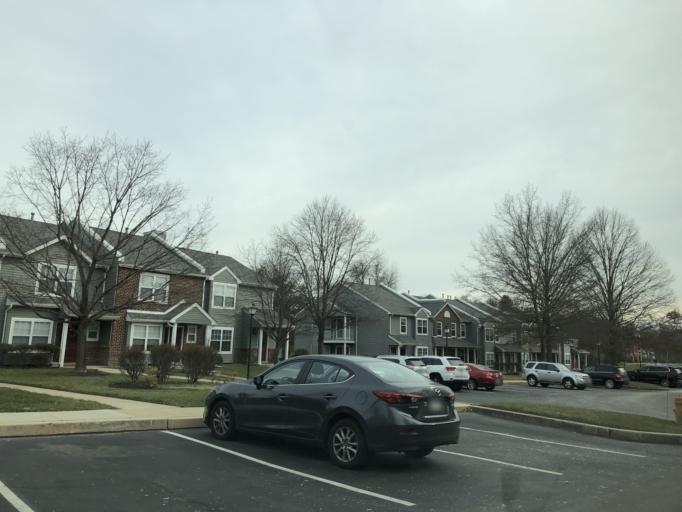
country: US
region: Pennsylvania
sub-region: Chester County
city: Exton
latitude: 40.0302
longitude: -75.6410
